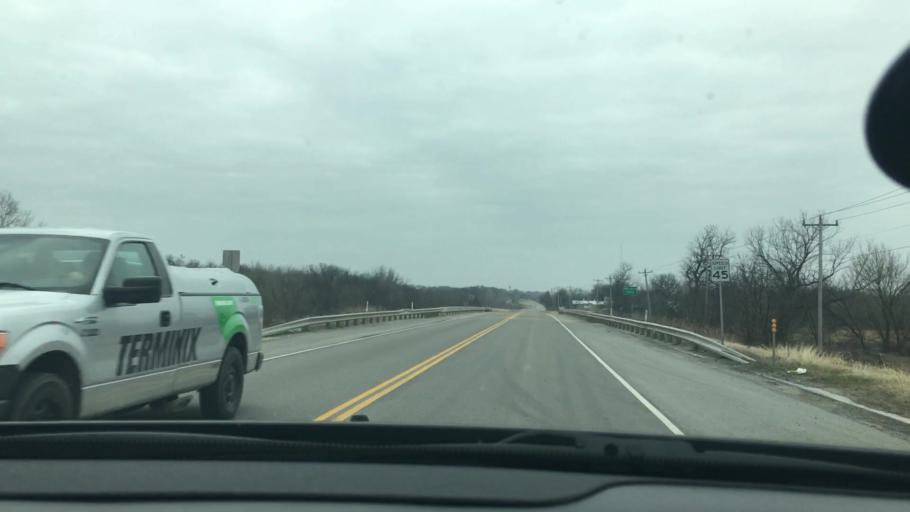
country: US
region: Oklahoma
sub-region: Carter County
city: Healdton
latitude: 34.2481
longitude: -97.4923
